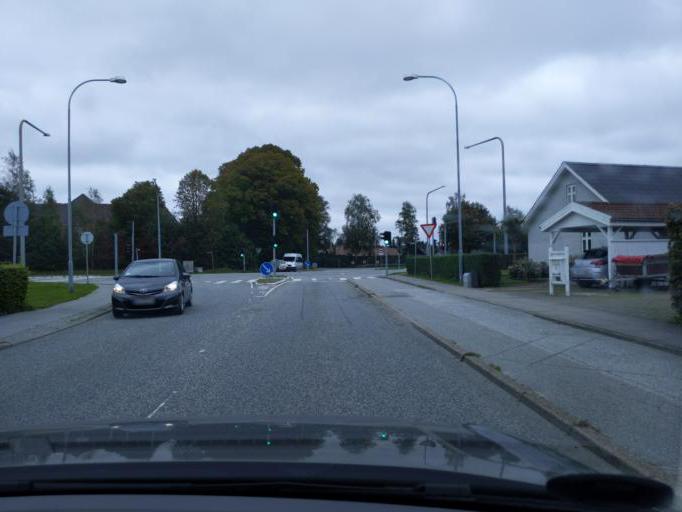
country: DK
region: Central Jutland
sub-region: Randers Kommune
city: Randers
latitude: 56.4799
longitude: 9.9988
